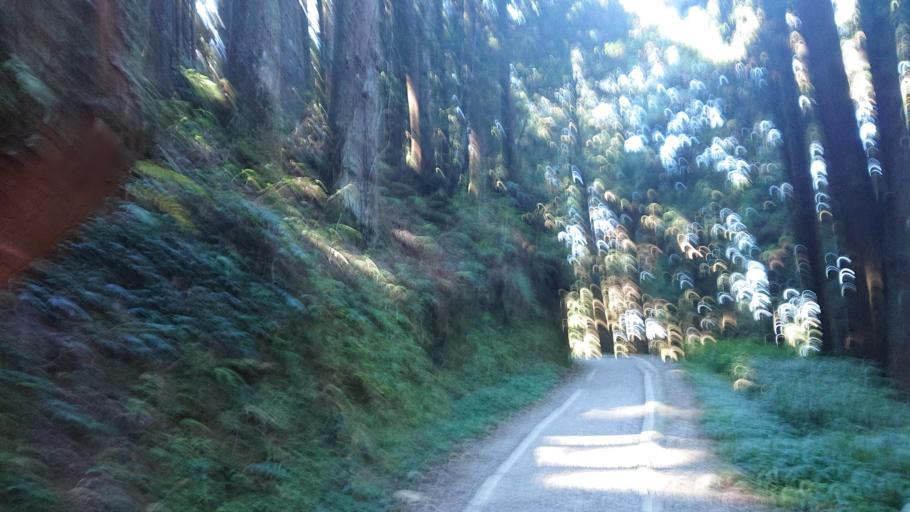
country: TW
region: Taiwan
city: Lugu
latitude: 23.4836
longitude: 120.8285
